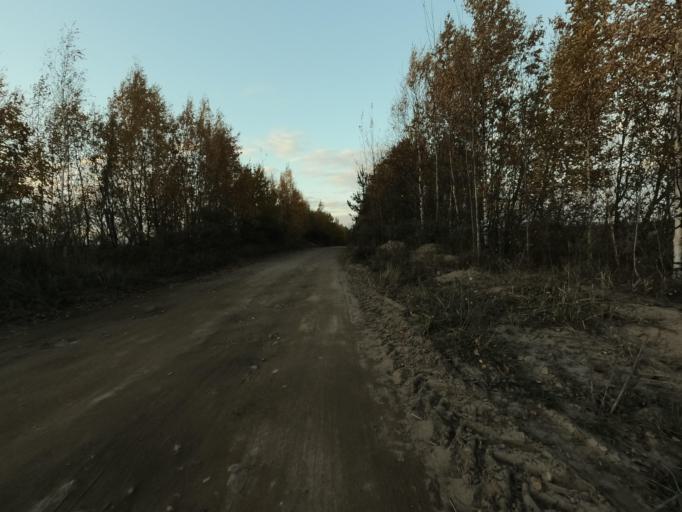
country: RU
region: Leningrad
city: Mga
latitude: 59.7898
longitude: 31.2017
